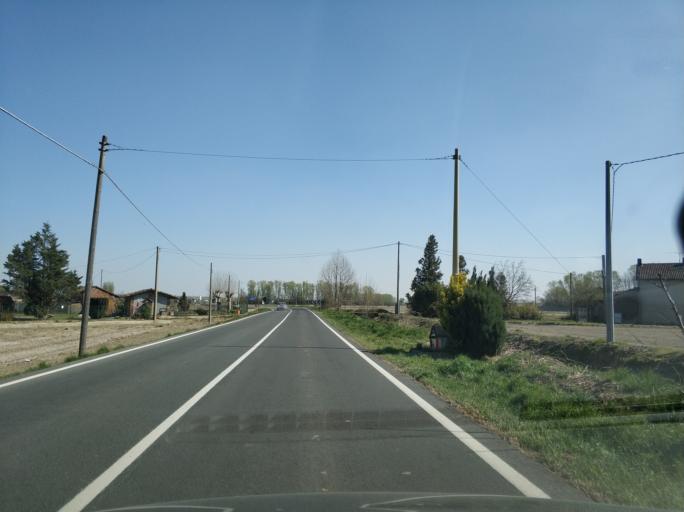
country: IT
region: Piedmont
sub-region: Provincia di Vercelli
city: Borgo Vercelli
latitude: 45.3291
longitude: 8.4620
